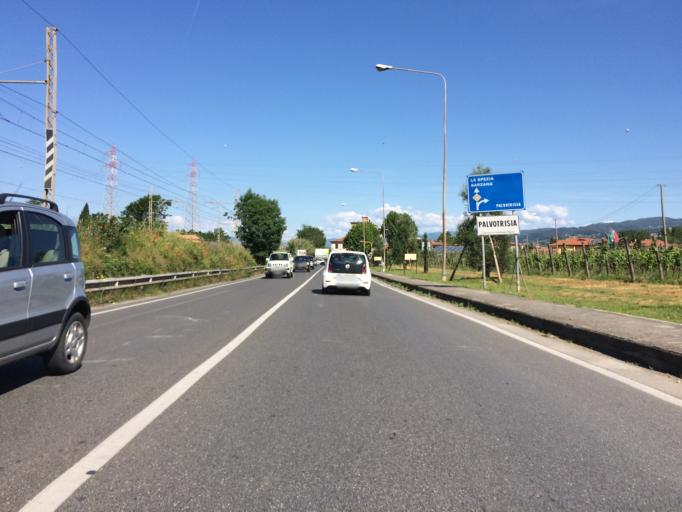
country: IT
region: Liguria
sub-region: Provincia di La Spezia
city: Colombiera-Molicciara
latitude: 44.0760
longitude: 10.0144
